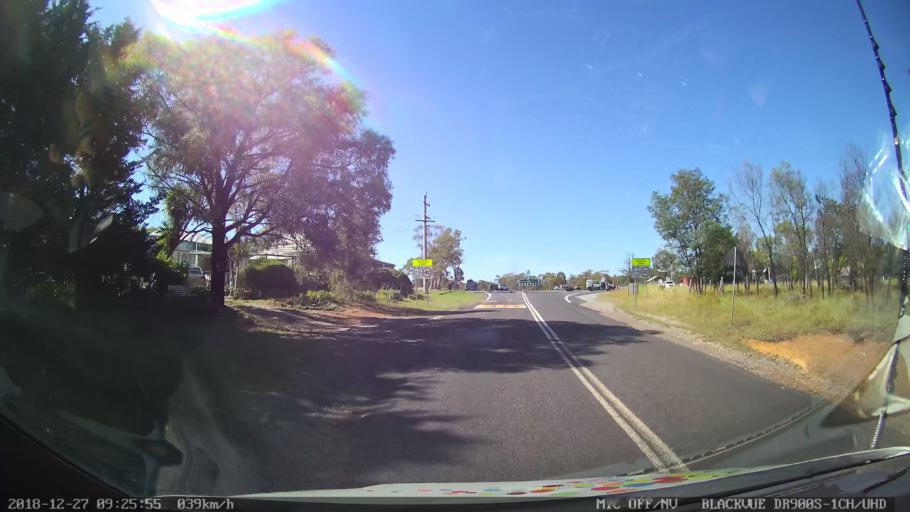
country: AU
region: New South Wales
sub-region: Lithgow
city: Portland
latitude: -33.1458
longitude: 149.9847
